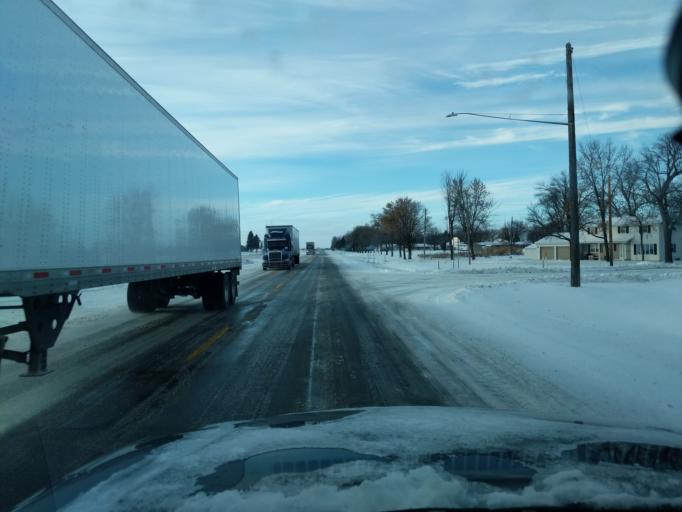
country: US
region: Minnesota
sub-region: Renville County
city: Hector
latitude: 44.7404
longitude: -94.7180
